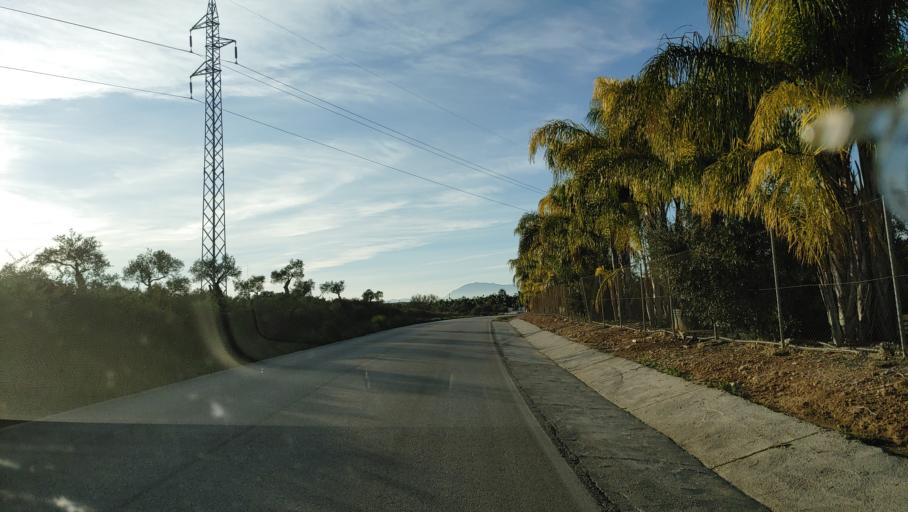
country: ES
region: Andalusia
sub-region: Provincia de Malaga
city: Cartama
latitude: 36.6789
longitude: -4.6212
